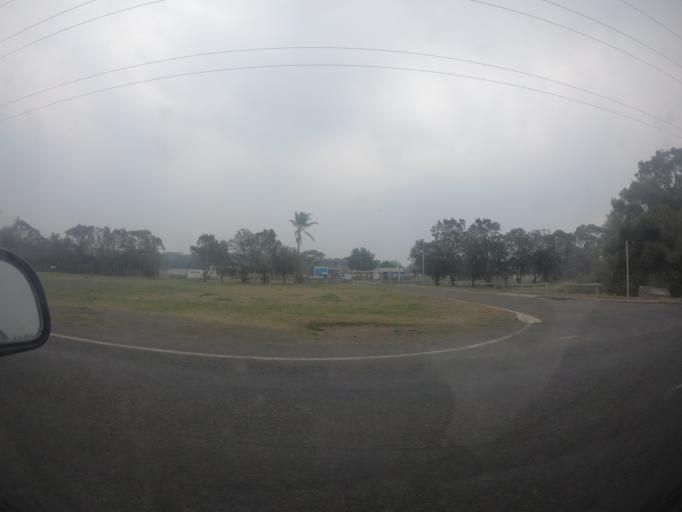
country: AU
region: New South Wales
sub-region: Shellharbour
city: Barrack Heights
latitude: -34.5699
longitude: 150.8664
